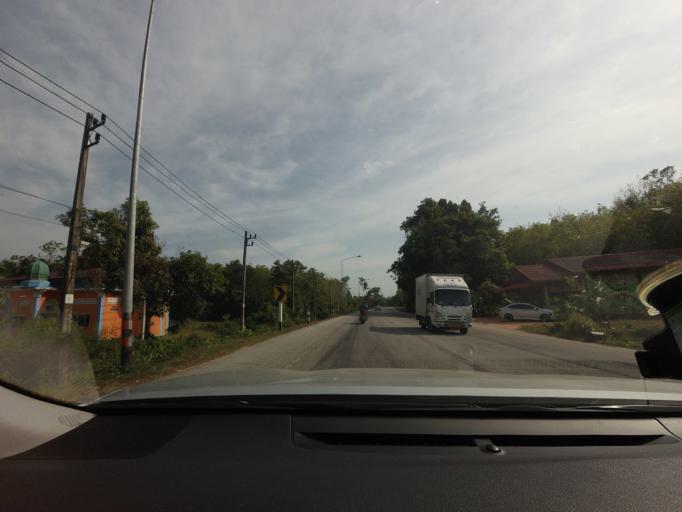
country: TH
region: Narathiwat
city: Narathiwat
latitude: 6.3594
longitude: 101.7912
